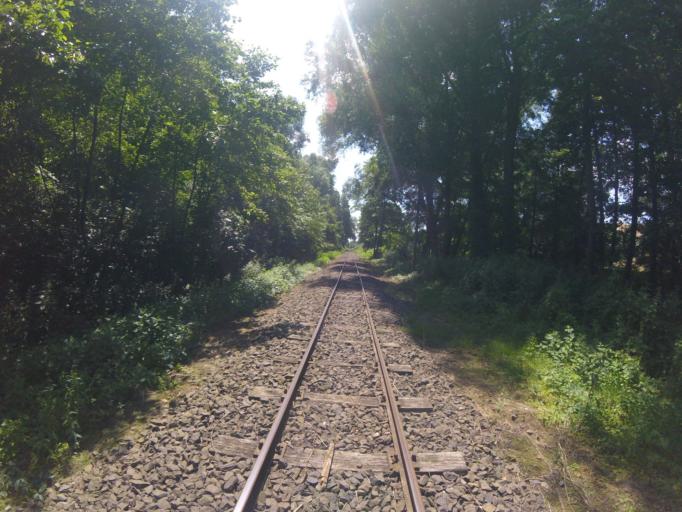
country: HU
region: Zala
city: Letenye
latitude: 46.5195
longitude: 16.7286
